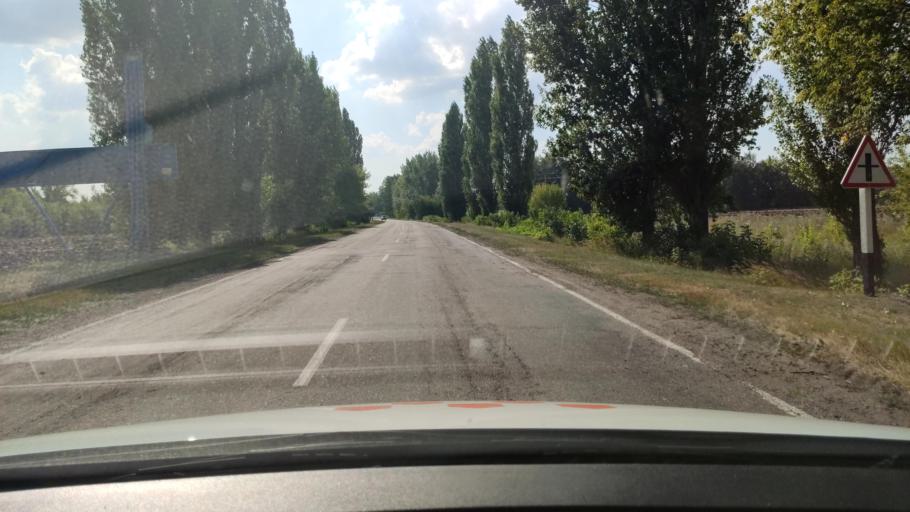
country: RU
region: Voronezj
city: Sadovoye
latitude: 51.7591
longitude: 40.4377
